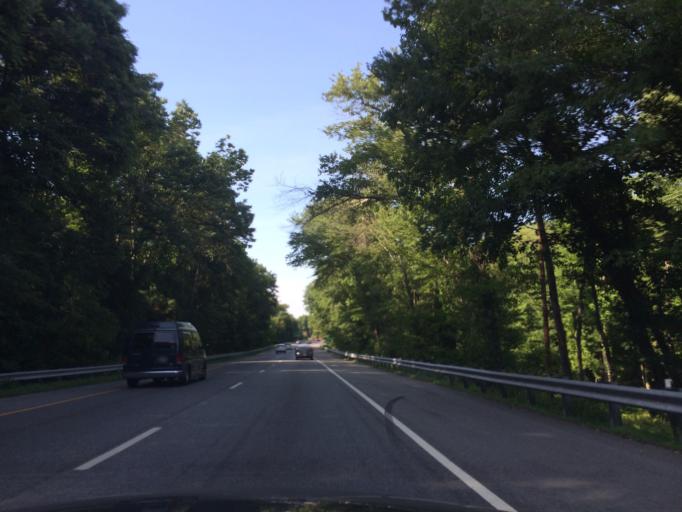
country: US
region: Maryland
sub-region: Anne Arundel County
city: Crofton
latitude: 38.9796
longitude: -76.7127
